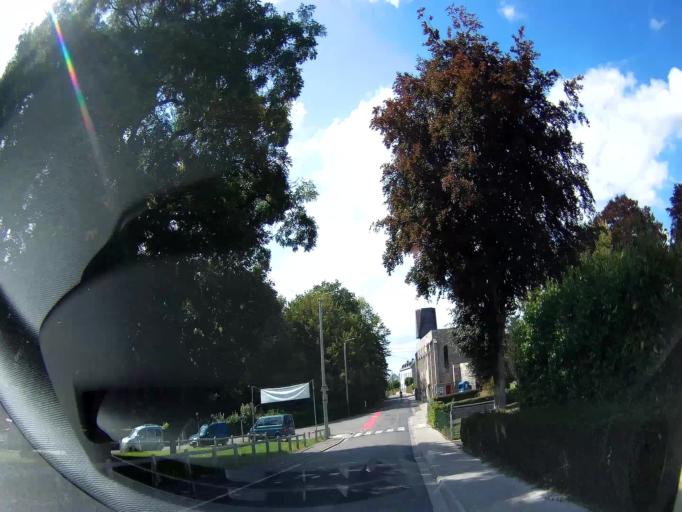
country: BE
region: Wallonia
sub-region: Province de Namur
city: Yvoir
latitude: 50.3532
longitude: 4.9027
